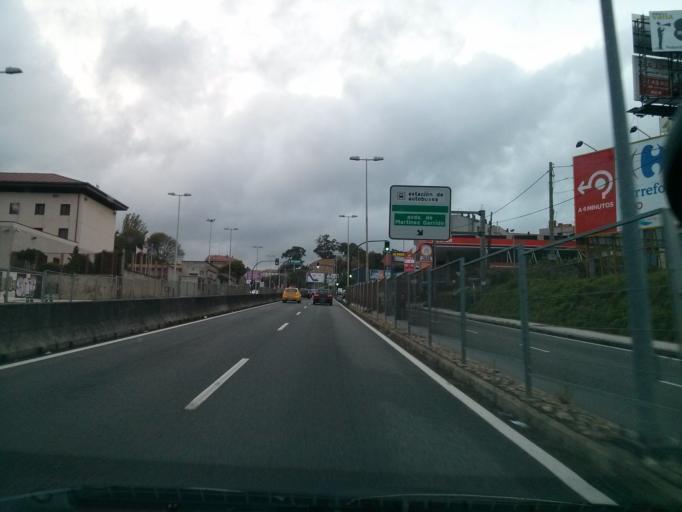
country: ES
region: Galicia
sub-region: Provincia de Pontevedra
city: Vigo
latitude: 42.2220
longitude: -8.7079
